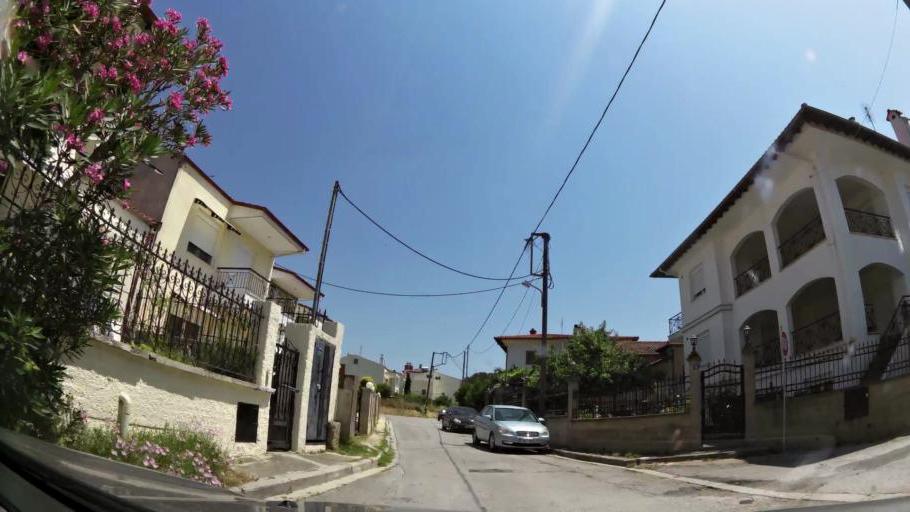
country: GR
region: Central Macedonia
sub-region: Nomos Thessalonikis
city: Trilofos
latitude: 40.4676
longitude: 22.9744
